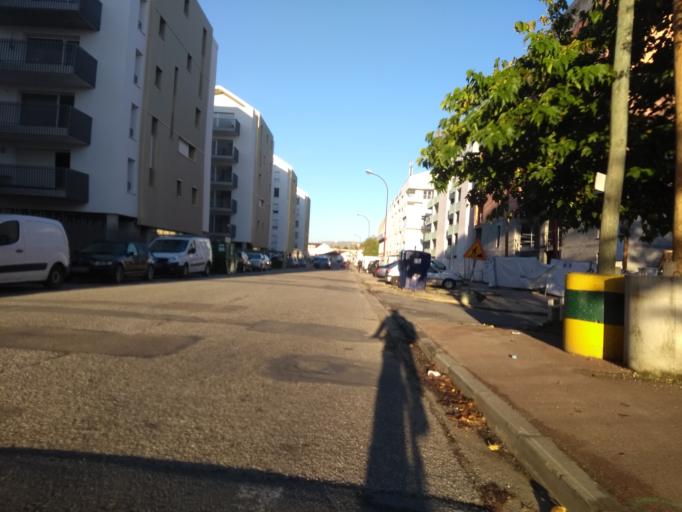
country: FR
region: Aquitaine
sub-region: Departement de la Gironde
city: Talence
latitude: 44.8049
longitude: -0.5897
